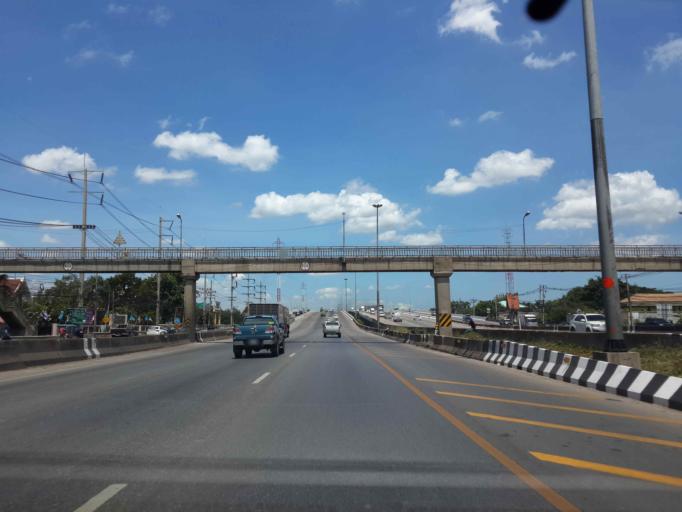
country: TH
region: Samut Sakhon
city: Samut Sakhon
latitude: 13.5435
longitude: 100.2455
